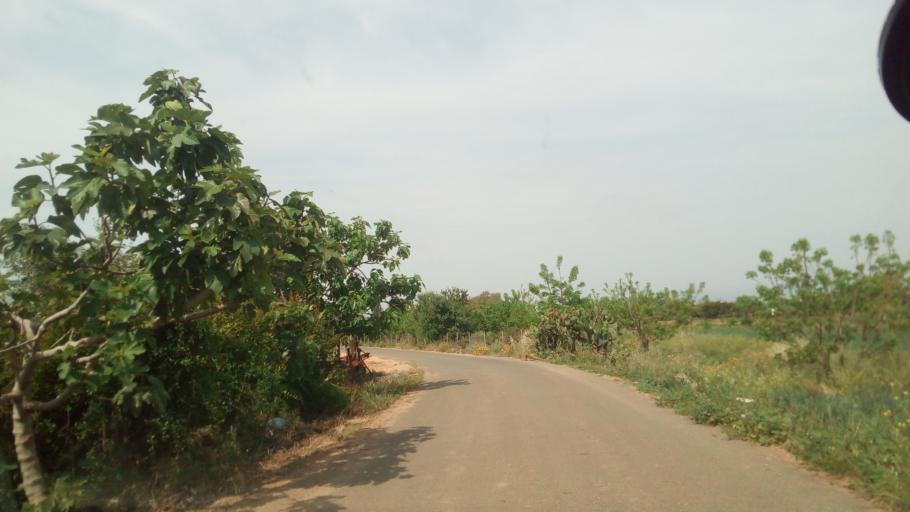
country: CY
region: Pafos
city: Empa
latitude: 34.8109
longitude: 32.4329
